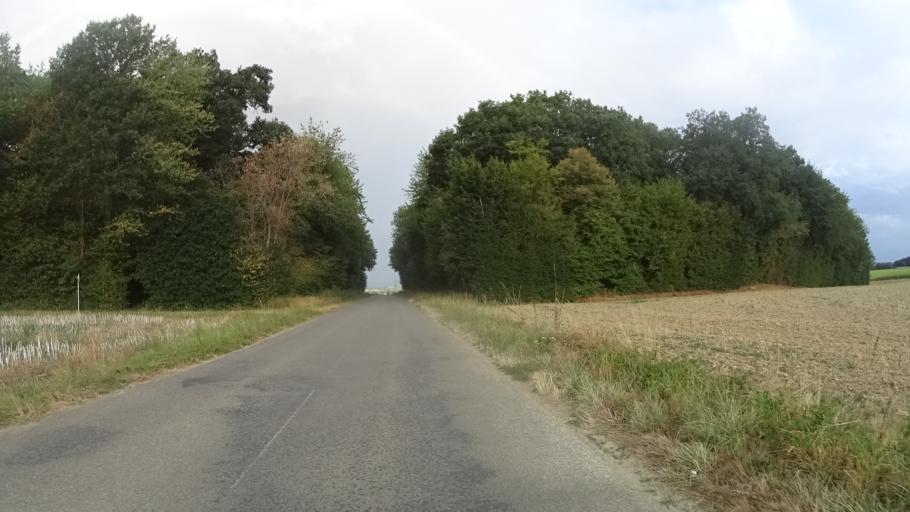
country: FR
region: Bourgogne
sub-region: Departement de Saone-et-Loire
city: Verdun-sur-le-Doubs
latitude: 46.9533
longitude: 5.0413
